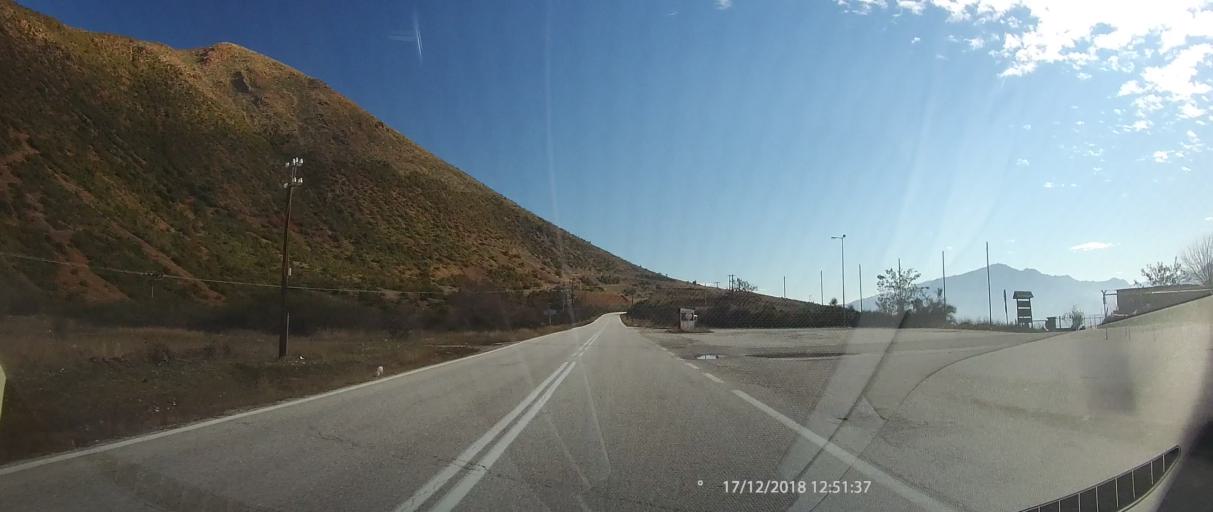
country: GR
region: Thessaly
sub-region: Trikala
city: Kastraki
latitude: 39.7645
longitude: 21.4680
